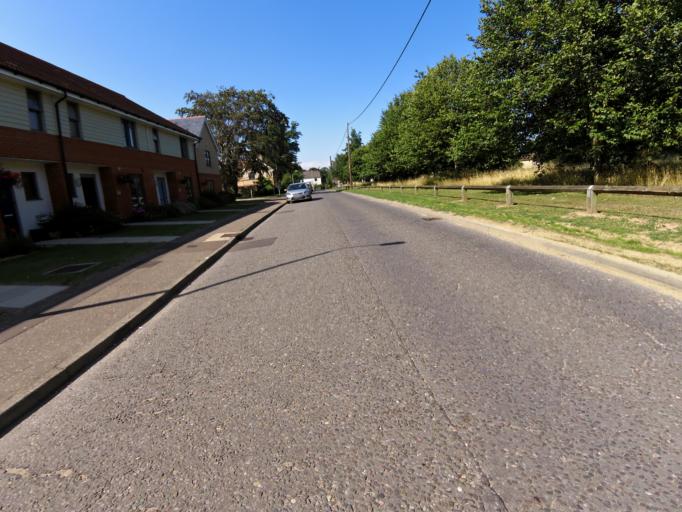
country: GB
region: England
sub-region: Essex
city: West Bergholt
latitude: 51.8882
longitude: 0.8472
